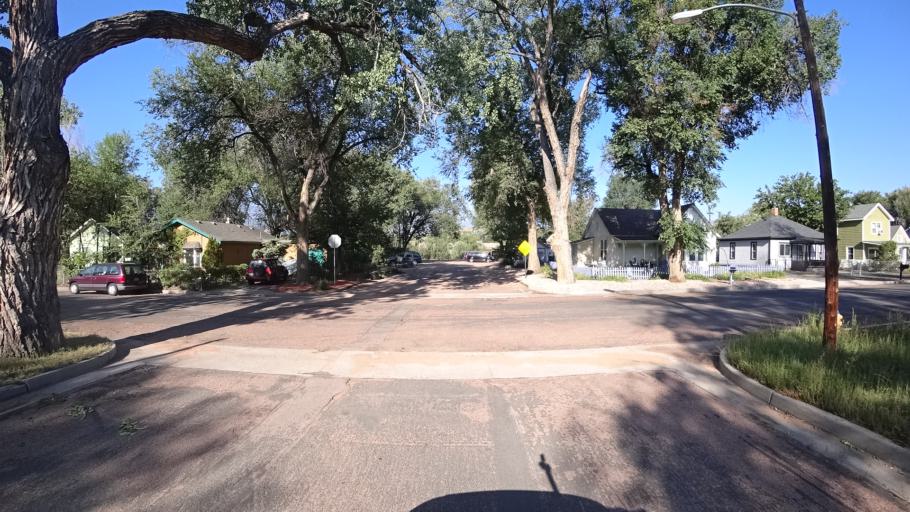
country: US
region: Colorado
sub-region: El Paso County
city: Colorado Springs
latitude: 38.8701
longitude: -104.8295
